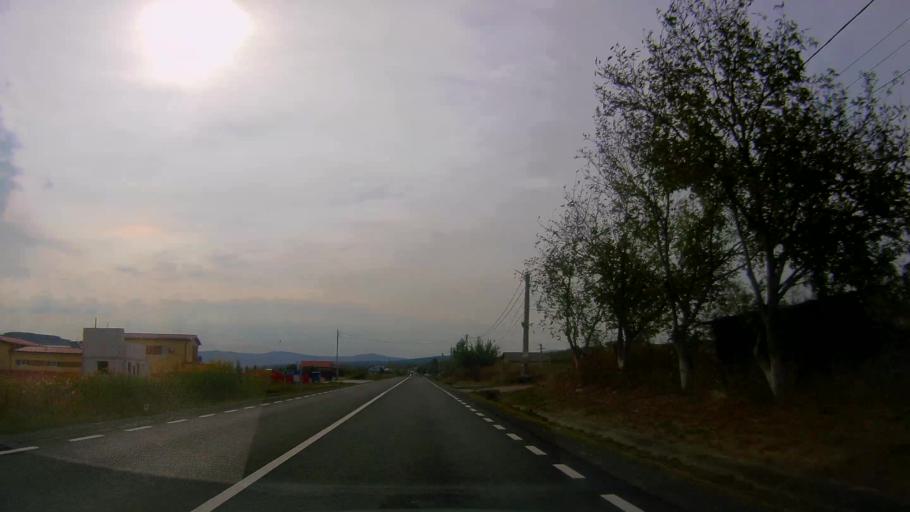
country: RO
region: Salaj
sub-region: Comuna Hereclean
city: Hereclean
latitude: 47.2513
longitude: 22.9829
